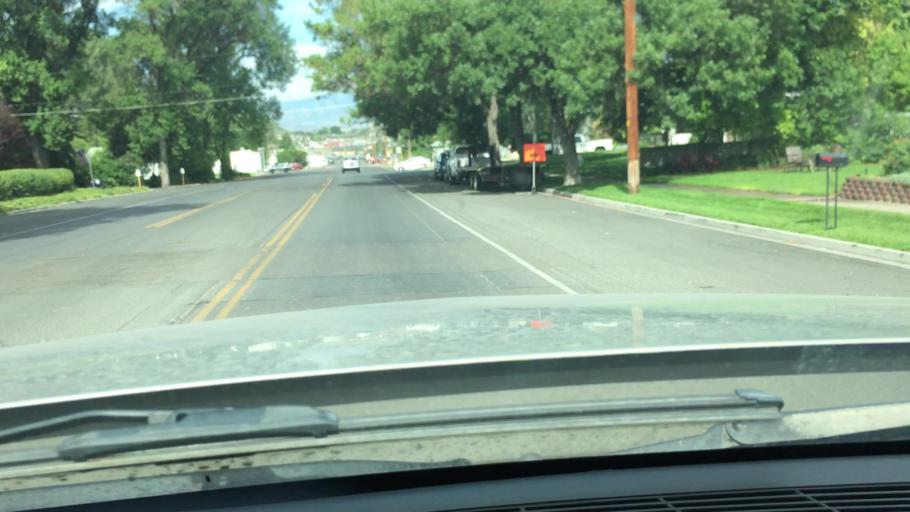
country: US
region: Utah
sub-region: Utah County
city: Pleasant Grove
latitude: 40.3613
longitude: -111.7413
